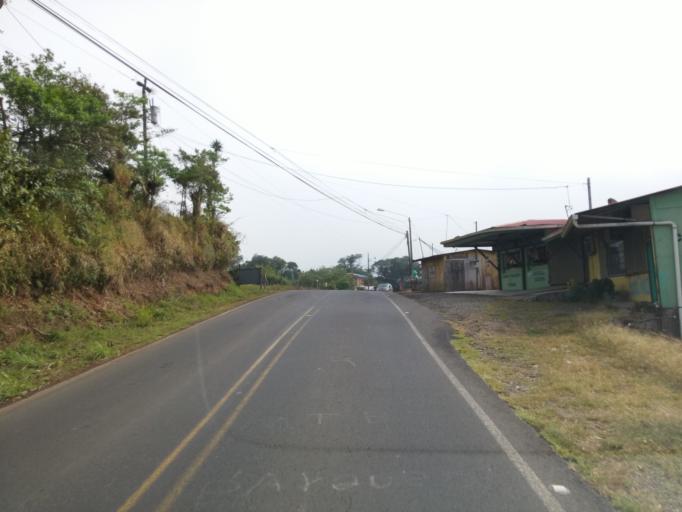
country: CR
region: Alajuela
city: San Ramon
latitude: 10.1467
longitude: -84.4865
